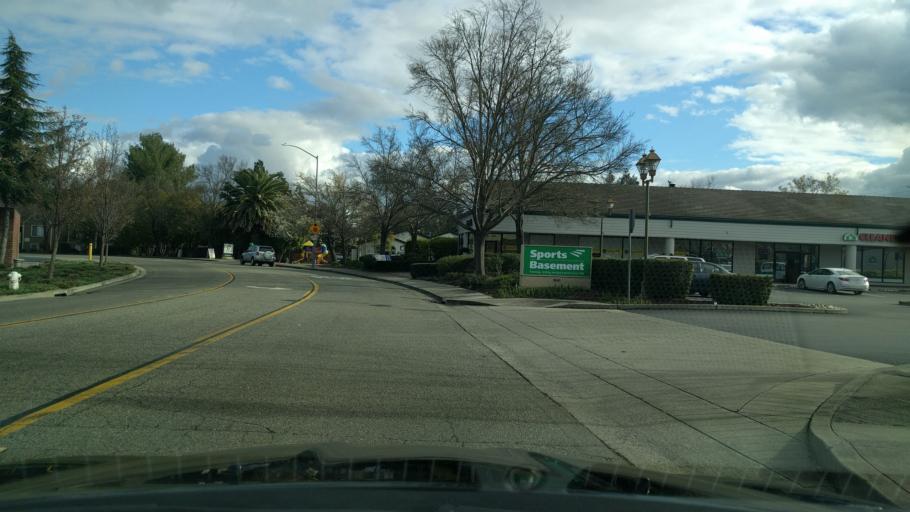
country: US
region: California
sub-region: Contra Costa County
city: San Ramon
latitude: 37.7625
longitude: -121.9523
